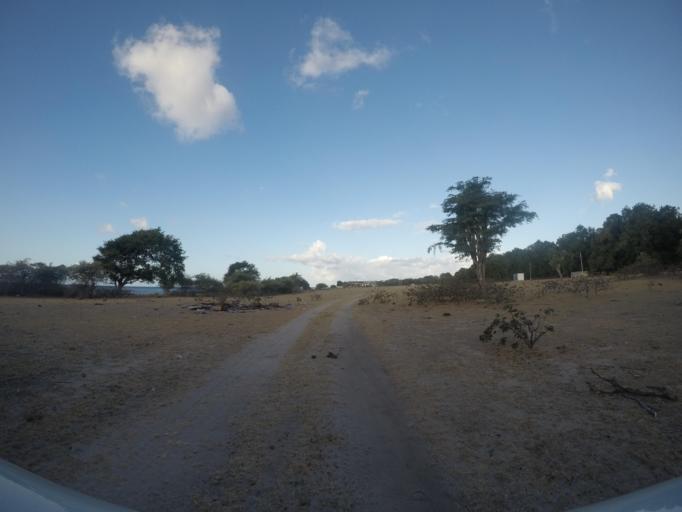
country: TL
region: Lautem
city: Lospalos
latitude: -8.3245
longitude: 126.9917
